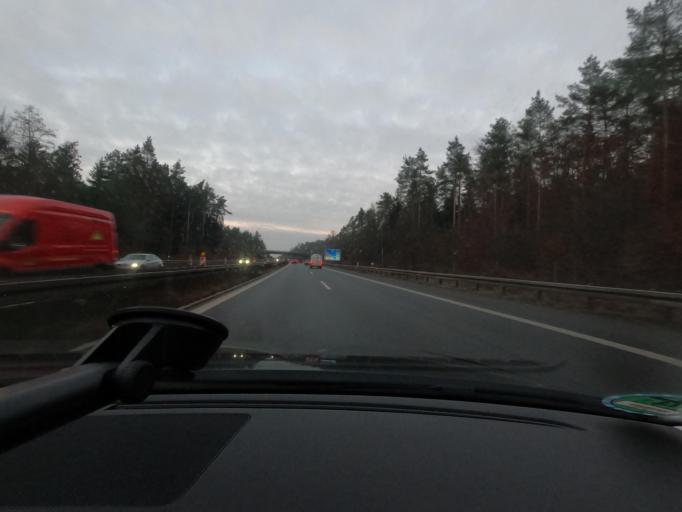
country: DE
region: Bavaria
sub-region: Upper Franconia
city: Memmelsdorf
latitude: 49.8862
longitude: 10.9494
